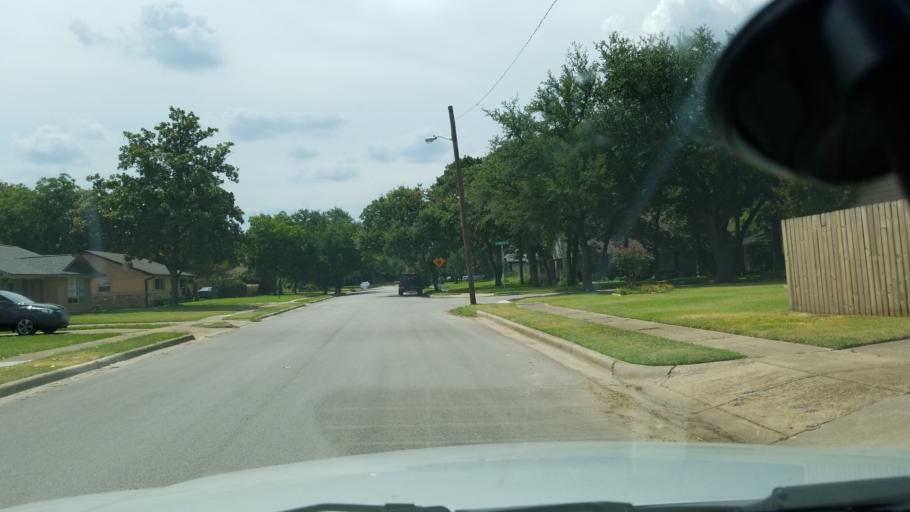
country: US
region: Texas
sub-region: Dallas County
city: Irving
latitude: 32.8185
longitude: -96.9833
